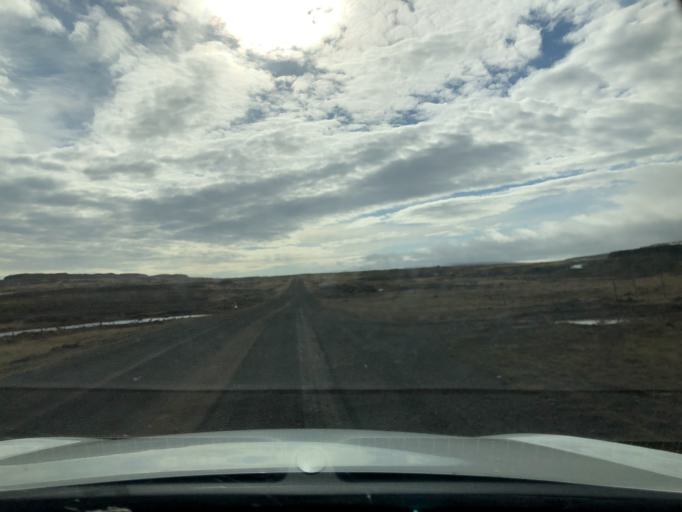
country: IS
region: West
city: Borgarnes
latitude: 65.0224
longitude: -22.0789
